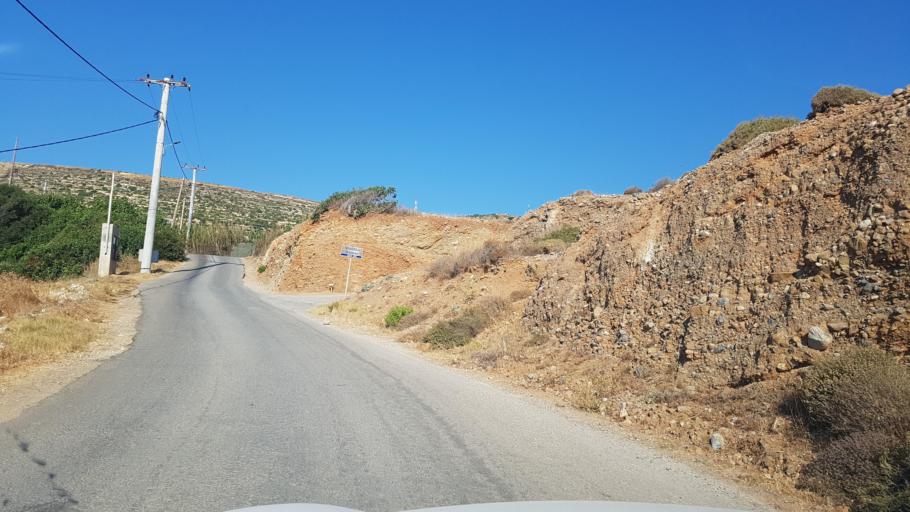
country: GR
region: Crete
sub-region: Nomos Chanias
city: Platanos
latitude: 35.4893
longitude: 23.5816
